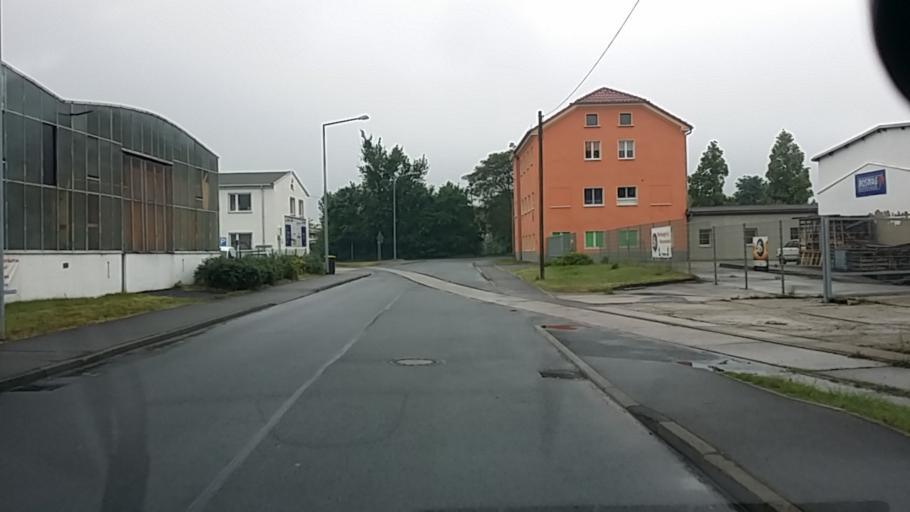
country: DE
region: Saxony
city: Ottendorf-Okrilla
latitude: 51.1813
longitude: 13.8289
